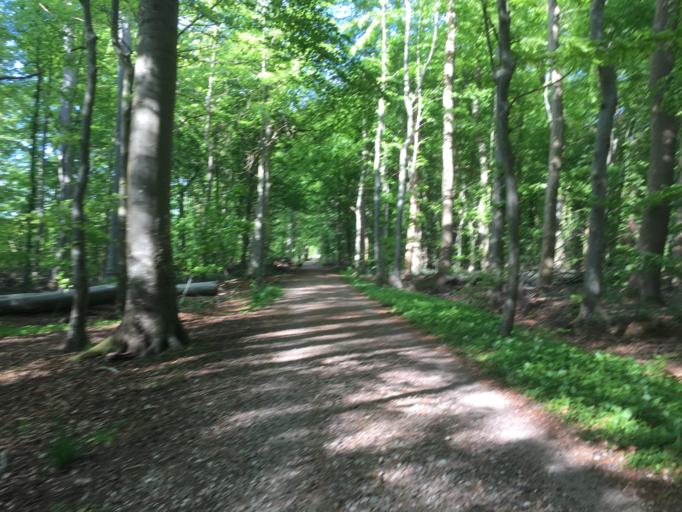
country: DK
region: South Denmark
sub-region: Odense Kommune
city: Hojby
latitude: 55.3505
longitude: 10.4355
